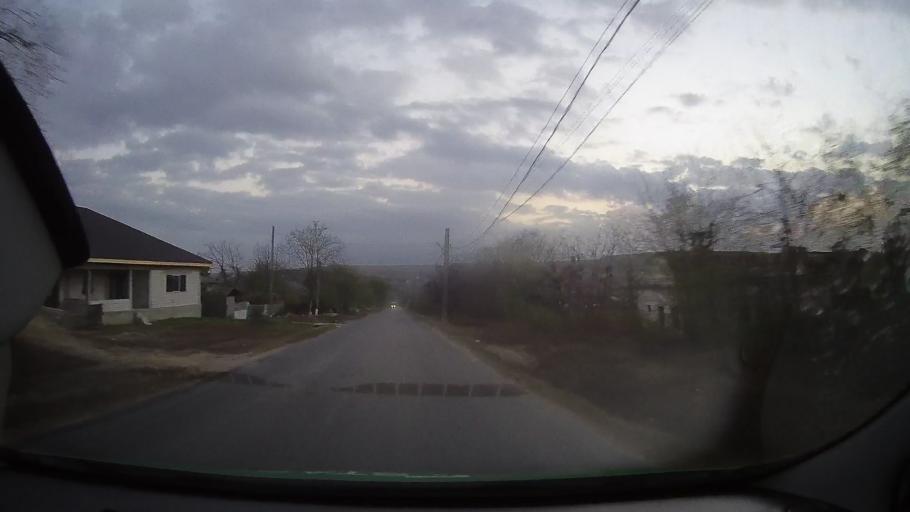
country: RO
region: Constanta
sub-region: Comuna Baneasa
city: Baneasa
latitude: 44.0753
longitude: 27.6960
